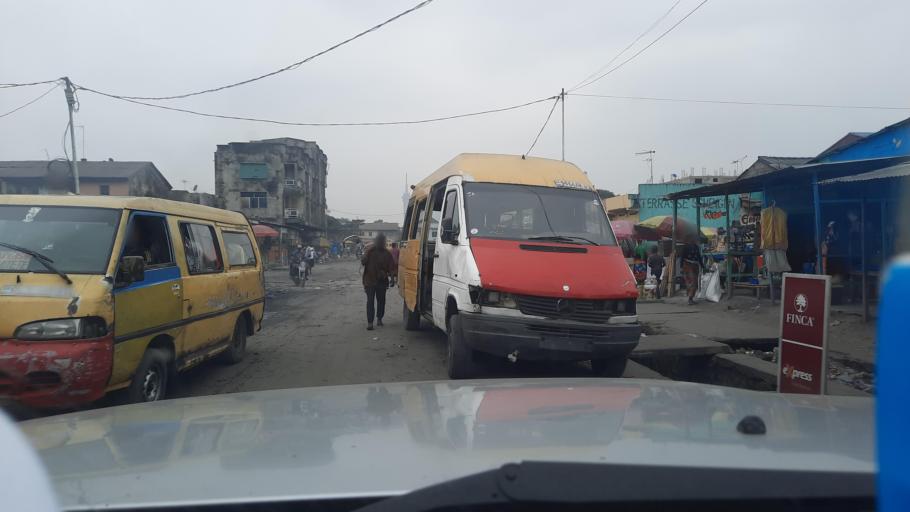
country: CD
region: Kinshasa
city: Masina
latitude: -4.3891
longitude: 15.3468
